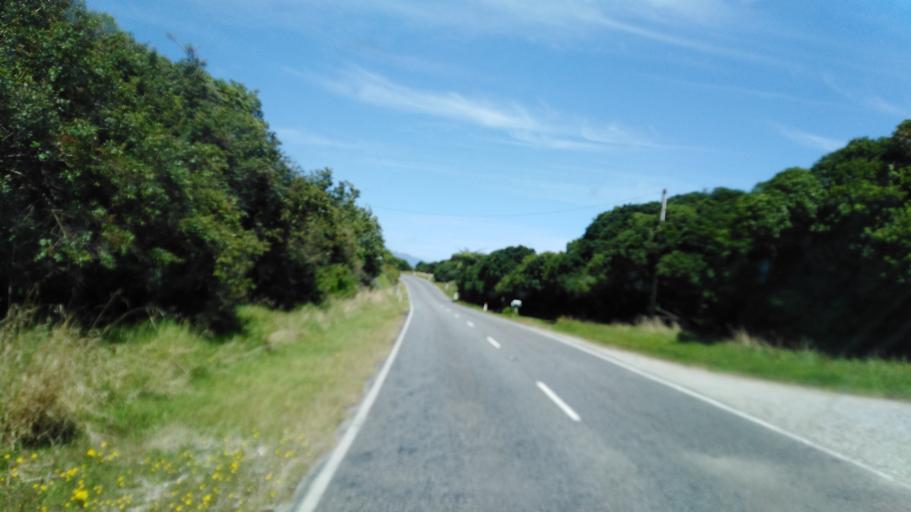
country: NZ
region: West Coast
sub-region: Buller District
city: Westport
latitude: -41.5756
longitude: 171.9015
